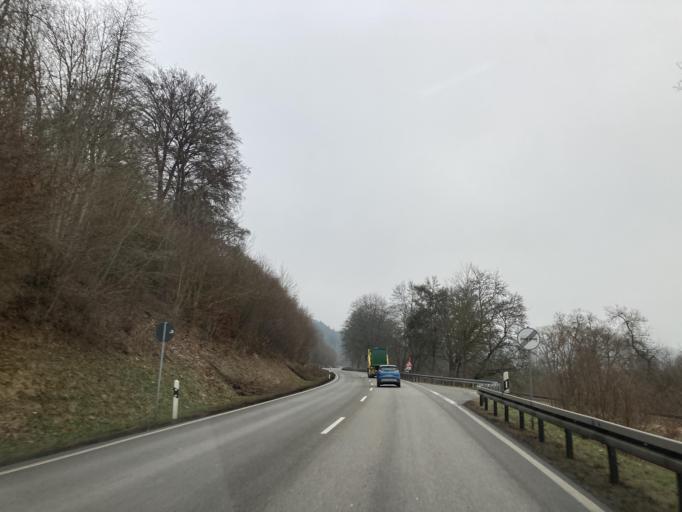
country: DE
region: Baden-Wuerttemberg
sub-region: Freiburg Region
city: Immendingen
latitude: 47.9414
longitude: 8.7602
